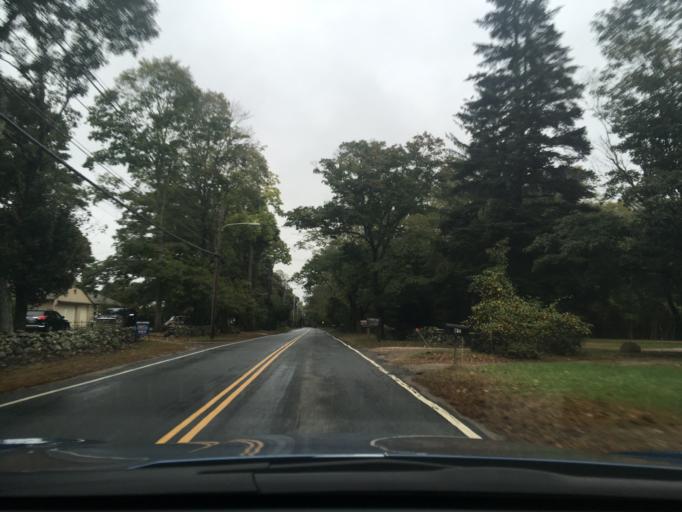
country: US
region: Rhode Island
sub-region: Kent County
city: East Greenwich
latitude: 41.6274
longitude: -71.4581
